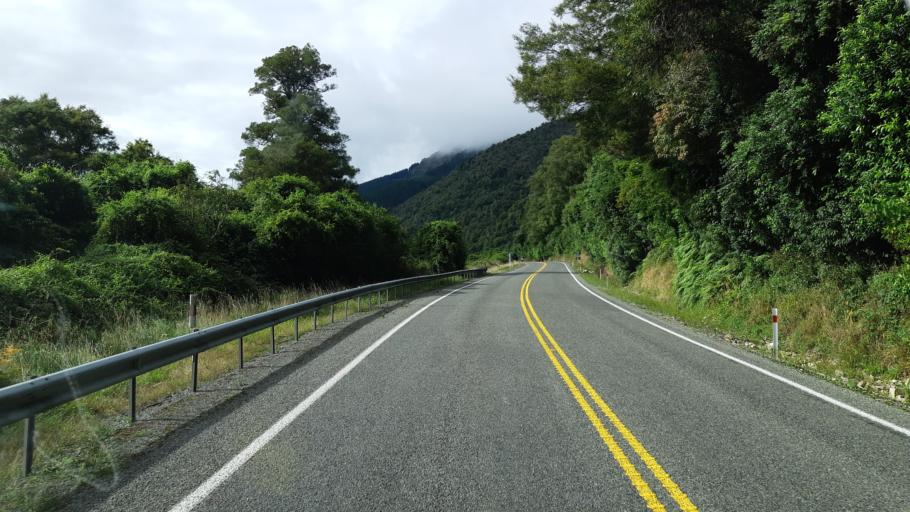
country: NZ
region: West Coast
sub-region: Buller District
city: Westport
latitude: -41.7697
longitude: 172.2358
